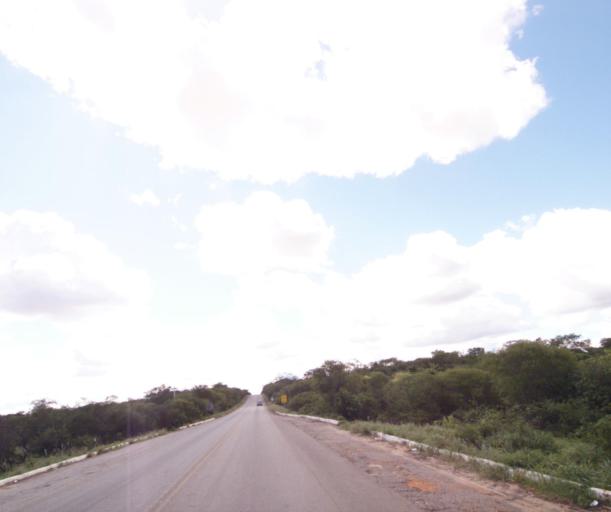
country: BR
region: Bahia
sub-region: Caetite
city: Caetite
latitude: -14.1696
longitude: -42.2304
